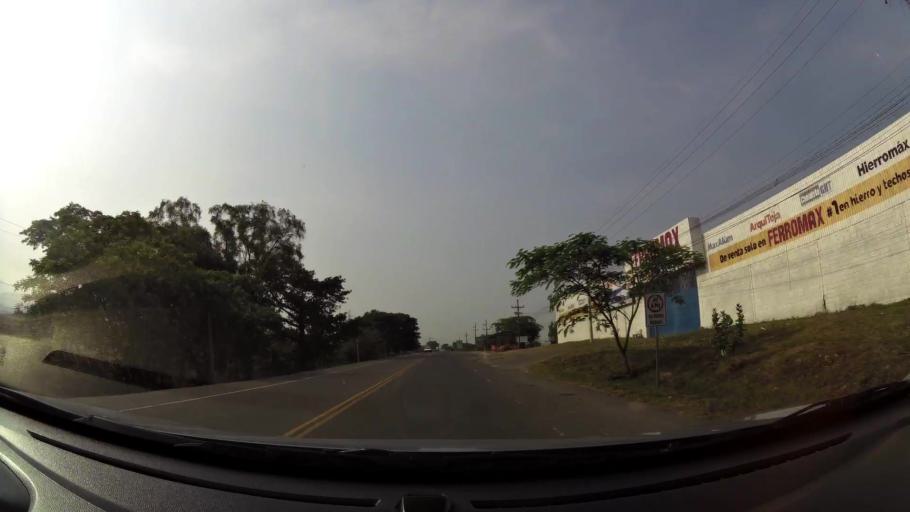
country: HN
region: Comayagua
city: Comayagua
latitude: 14.4285
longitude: -87.6303
